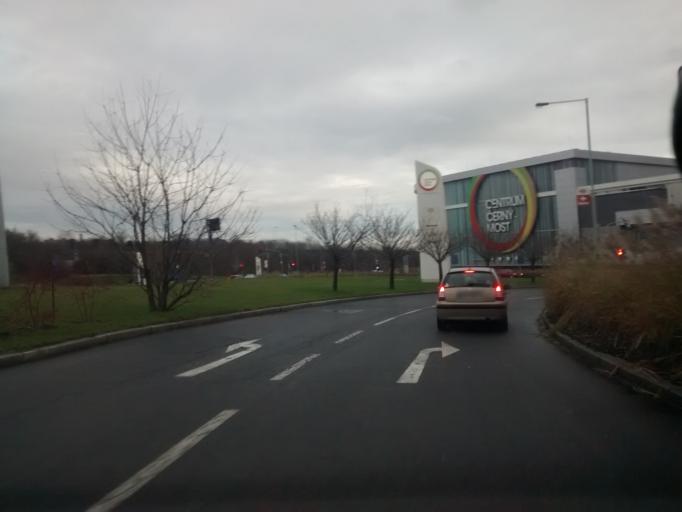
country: CZ
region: Praha
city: Cerny Most
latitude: 50.1100
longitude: 14.5837
